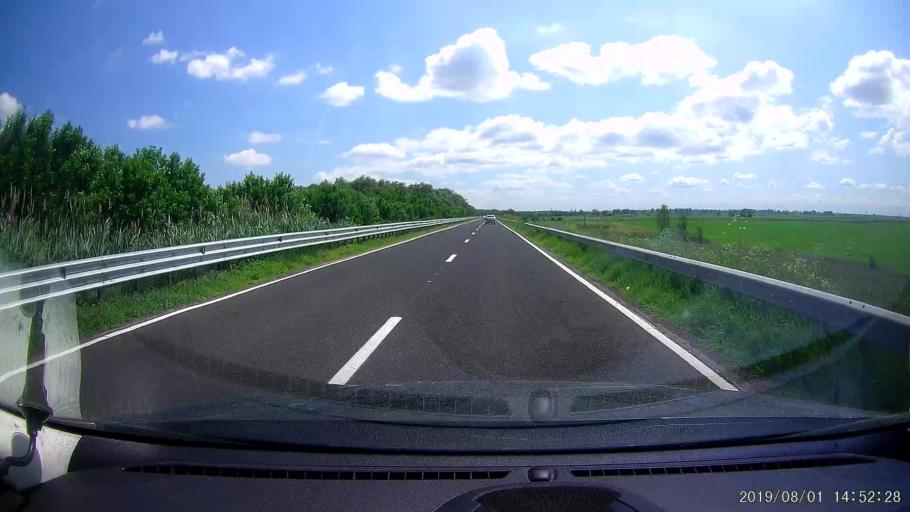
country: RO
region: Braila
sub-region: Comuna Vadeni
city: Vadeni
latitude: 45.3544
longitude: 28.0110
